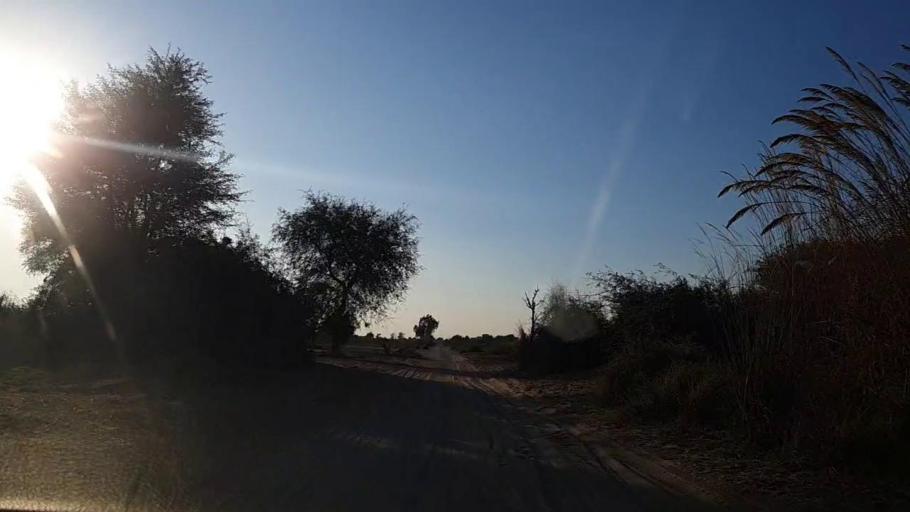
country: PK
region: Sindh
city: Khadro
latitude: 26.2790
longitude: 68.8450
